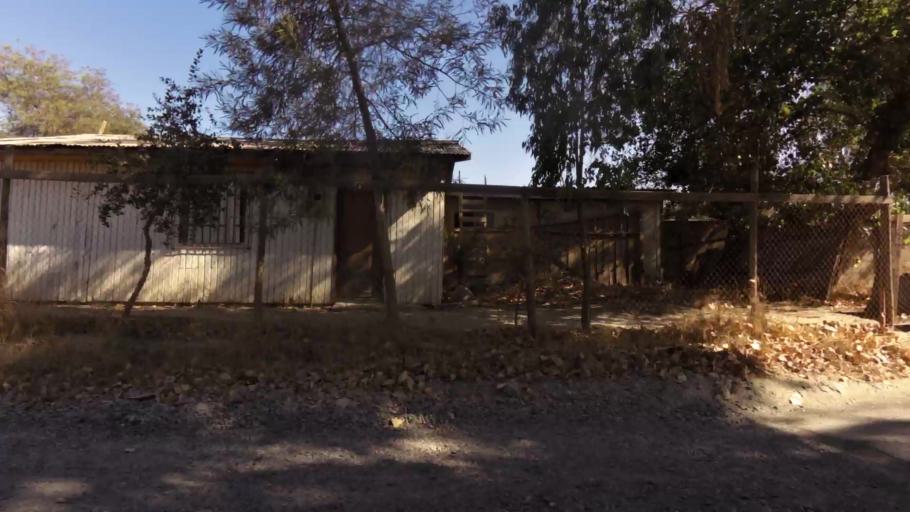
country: CL
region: Maule
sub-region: Provincia de Talca
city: Talca
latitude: -35.3987
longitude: -71.6222
